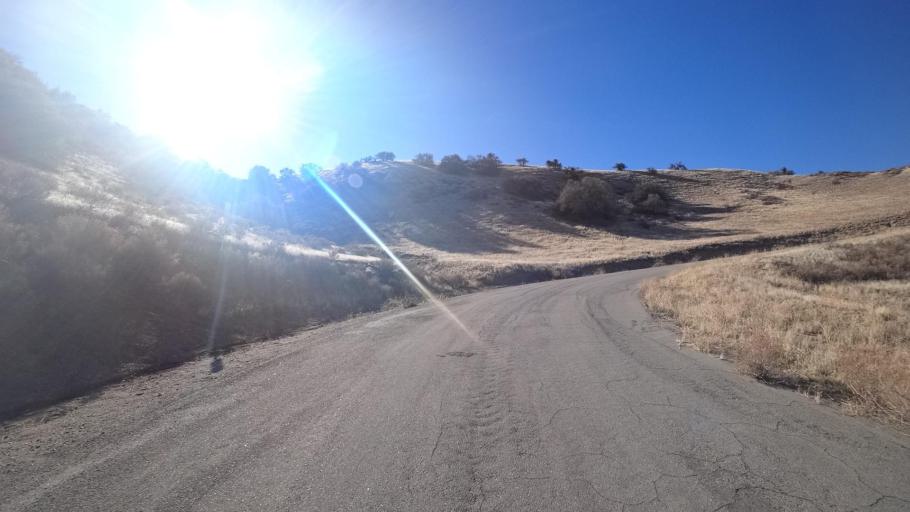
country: US
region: California
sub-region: Kern County
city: Maricopa
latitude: 34.9417
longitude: -119.4029
